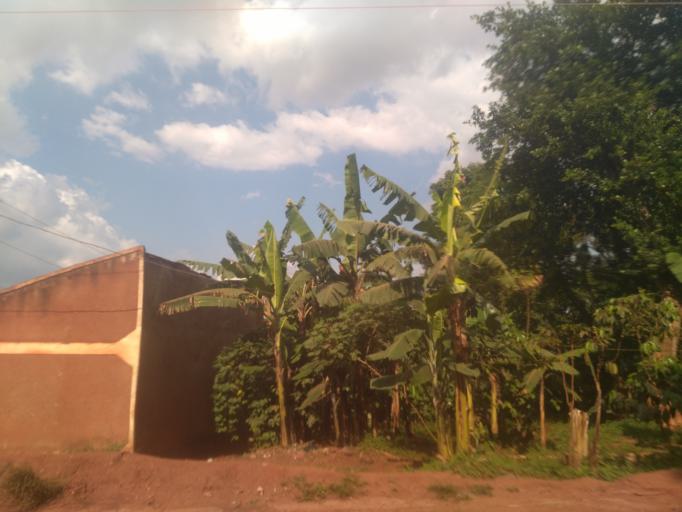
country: UG
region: Central Region
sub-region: Wakiso District
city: Kajansi
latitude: 0.2629
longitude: 32.4393
